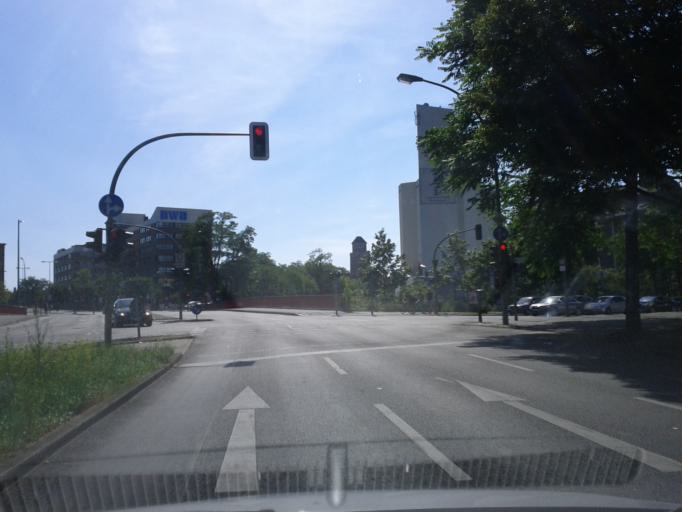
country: DE
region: Berlin
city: Wedding Bezirk
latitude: 52.5394
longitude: 13.3453
